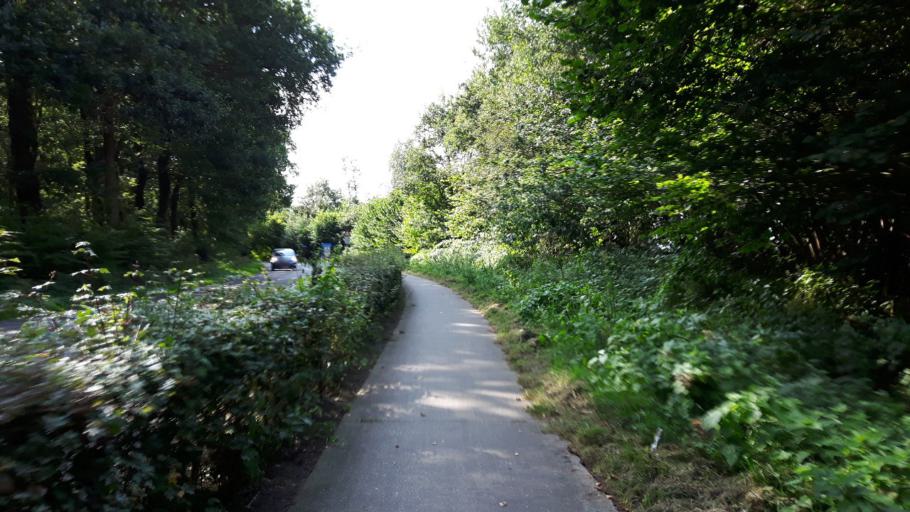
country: NL
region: Groningen
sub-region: Gemeente Leek
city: Leek
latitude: 53.1199
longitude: 6.4486
